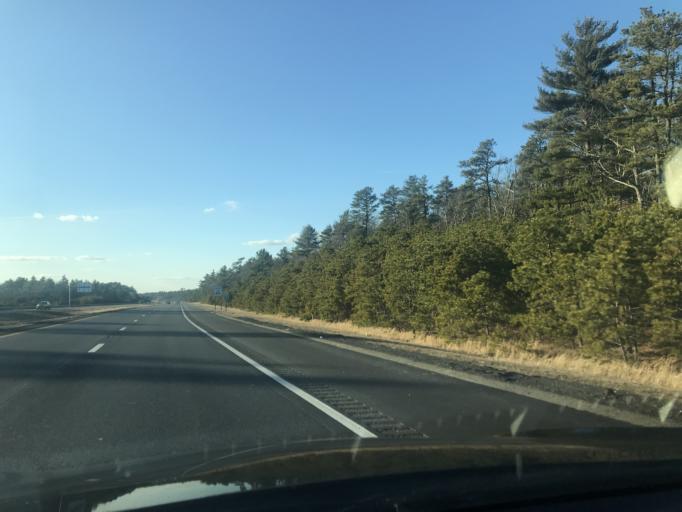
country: US
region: Massachusetts
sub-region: Plymouth County
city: Kingston
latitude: 41.9587
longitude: -70.7233
